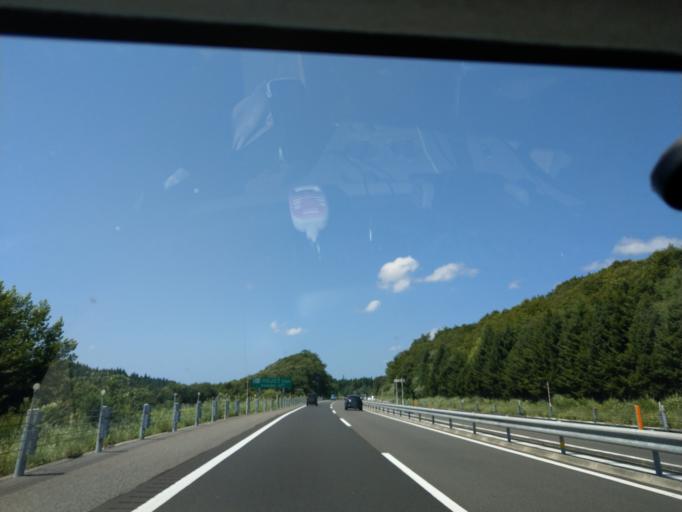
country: JP
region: Akita
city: Akita
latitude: 39.6266
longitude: 140.2318
